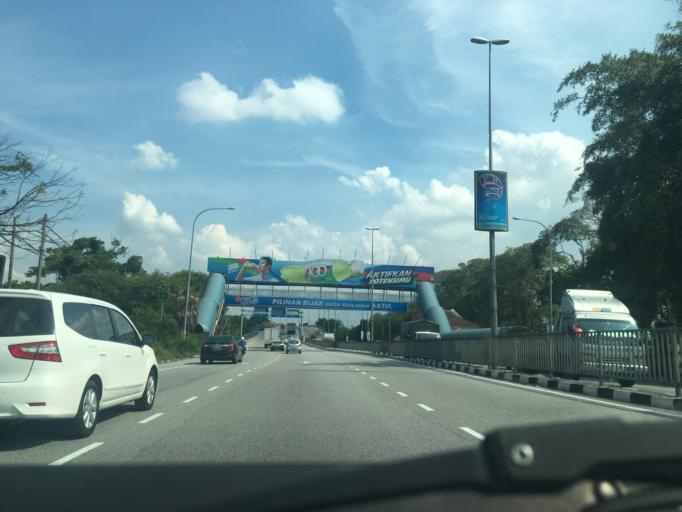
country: MY
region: Perak
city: Ipoh
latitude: 4.6140
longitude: 101.0791
